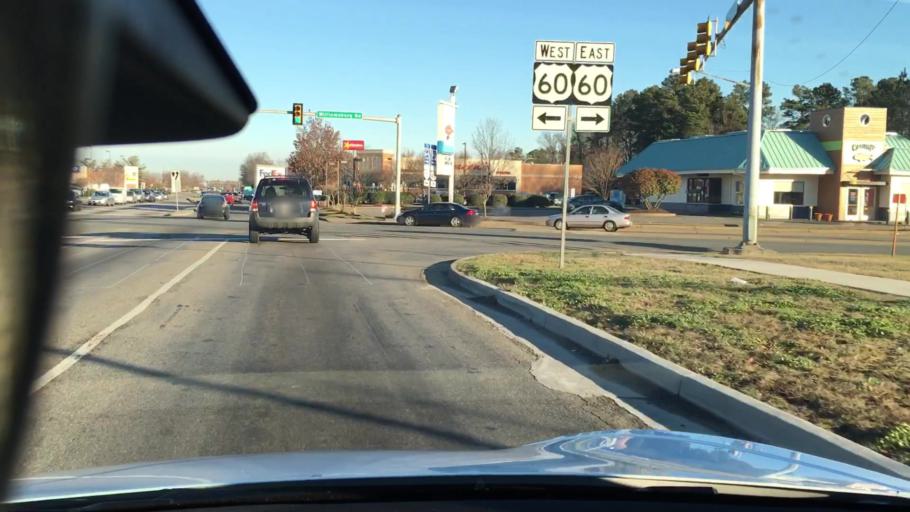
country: US
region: Virginia
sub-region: Henrico County
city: Fort Lee
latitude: 37.5169
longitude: -77.3498
